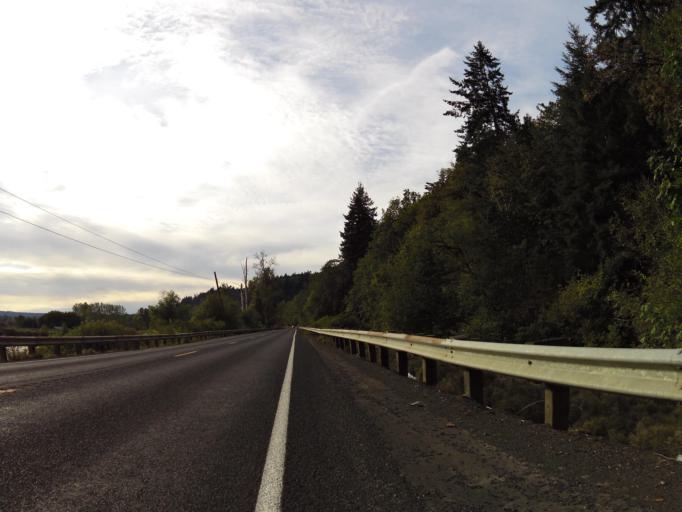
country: US
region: Washington
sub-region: Cowlitz County
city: West Longview
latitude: 46.1852
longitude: -123.0816
